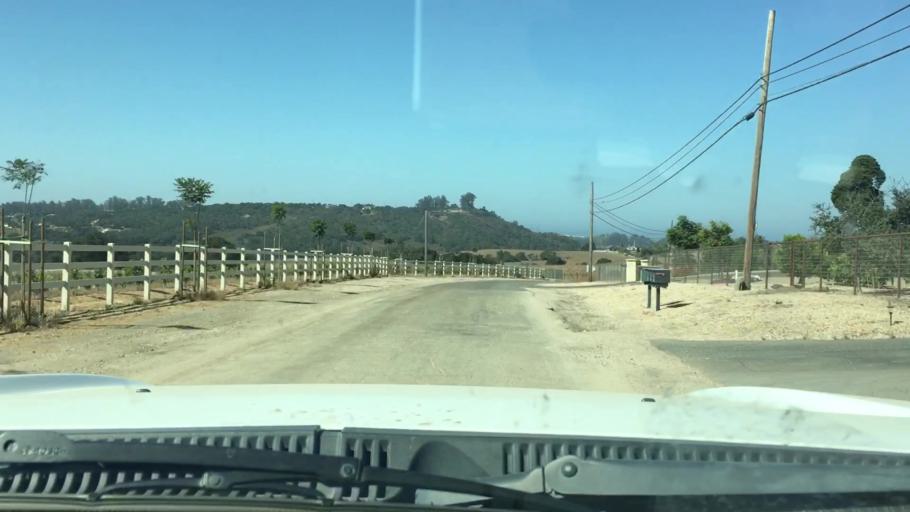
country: US
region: California
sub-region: San Luis Obispo County
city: Arroyo Grande
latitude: 35.1046
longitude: -120.5561
